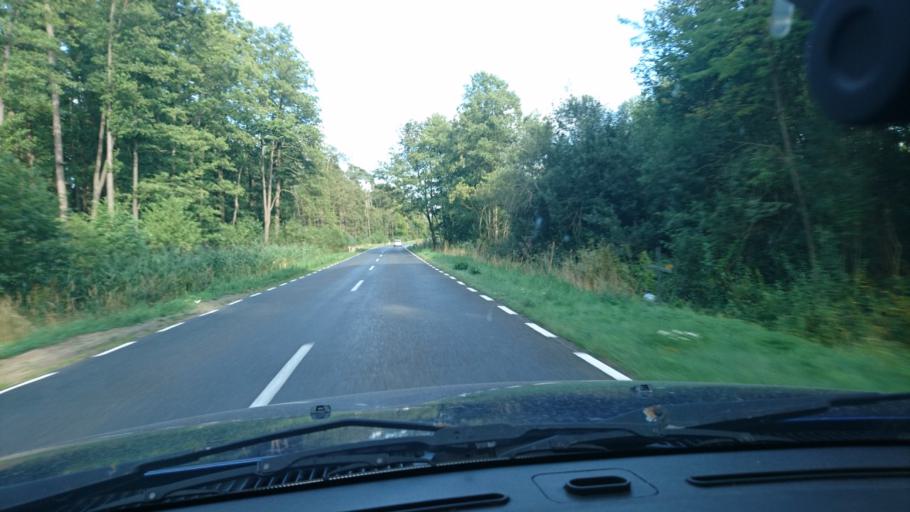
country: PL
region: Greater Poland Voivodeship
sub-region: Powiat krotoszynski
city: Sulmierzyce
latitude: 51.6020
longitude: 17.5865
